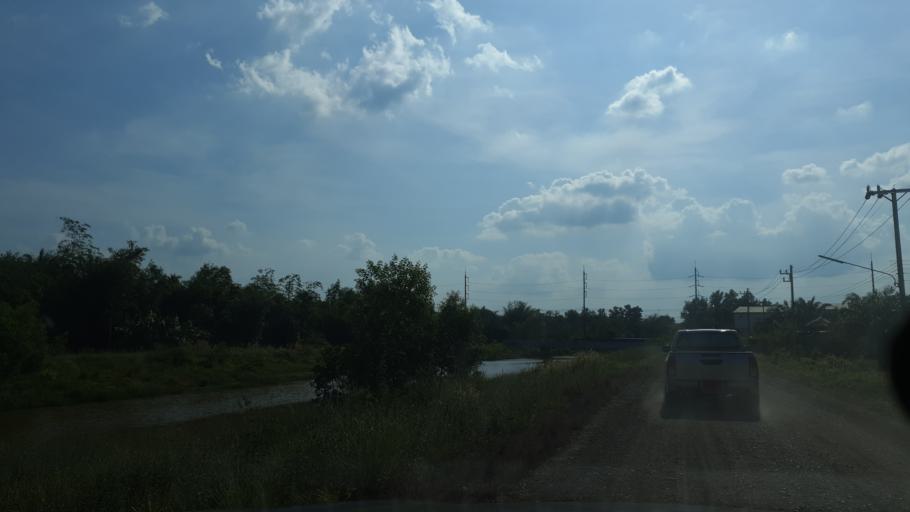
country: TH
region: Surat Thani
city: Phunphin
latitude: 9.1429
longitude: 99.1589
